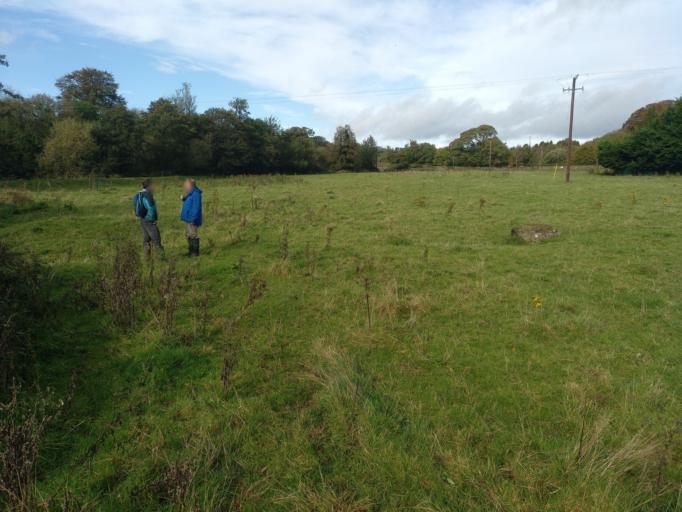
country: IE
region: Leinster
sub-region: Kilkenny
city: Castlecomer
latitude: 52.7936
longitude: -7.2069
